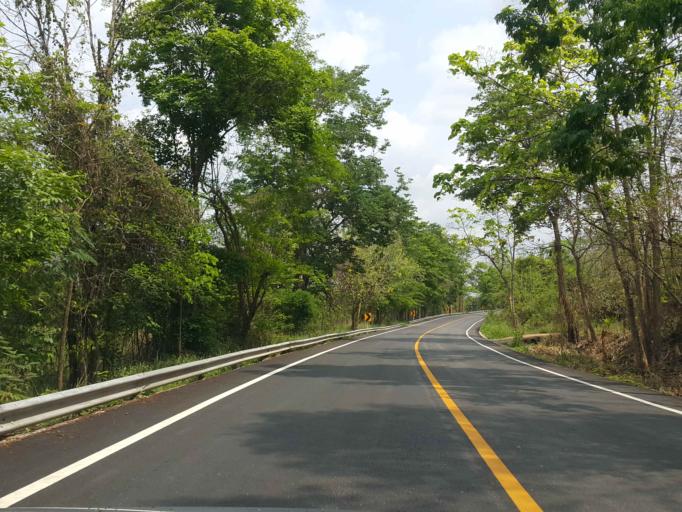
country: TH
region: Lampang
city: Thoen
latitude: 17.5554
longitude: 99.3373
